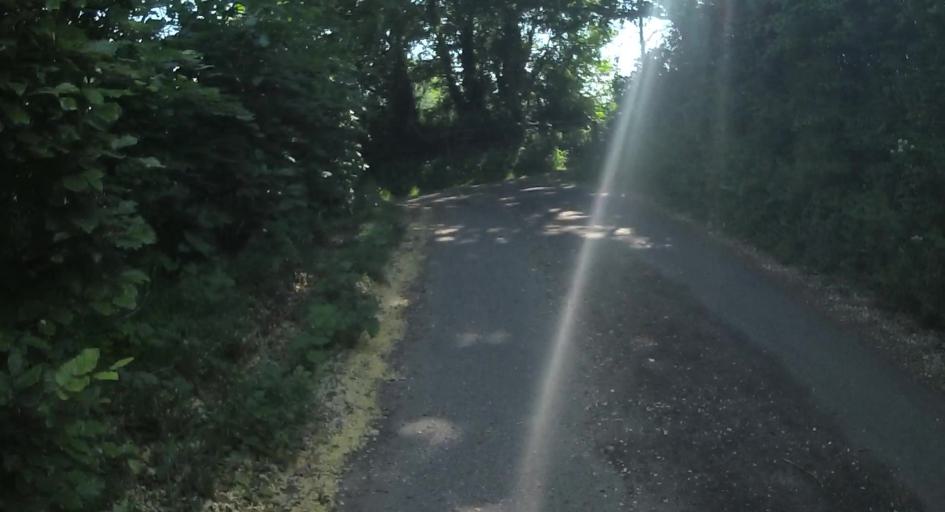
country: GB
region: England
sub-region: Hampshire
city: Kingsclere
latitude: 51.3558
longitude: -1.2756
